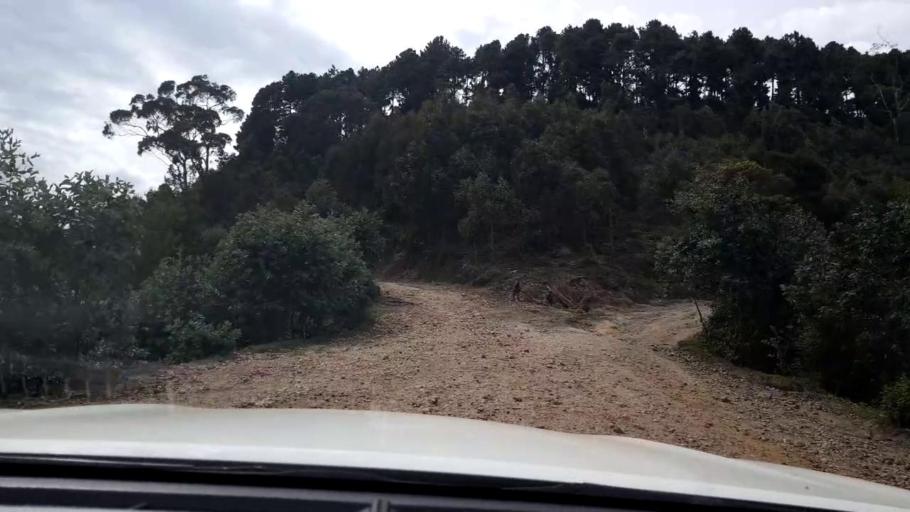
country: RW
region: Western Province
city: Kibuye
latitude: -1.8780
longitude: 29.4540
